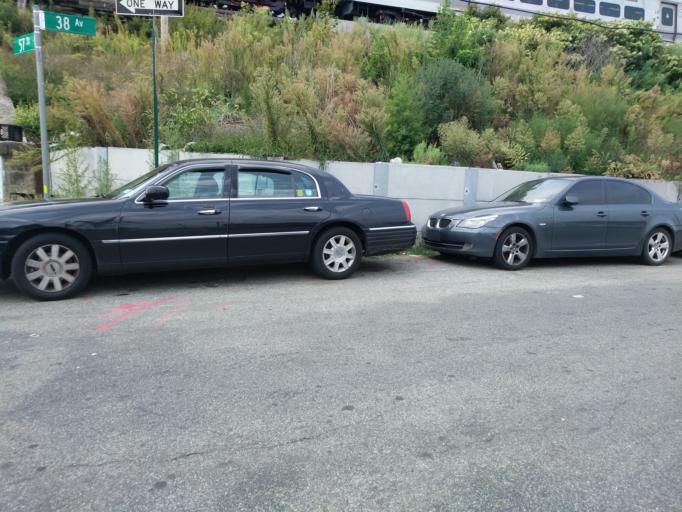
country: US
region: New York
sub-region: Queens County
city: Long Island City
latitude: 40.7489
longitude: -73.9060
